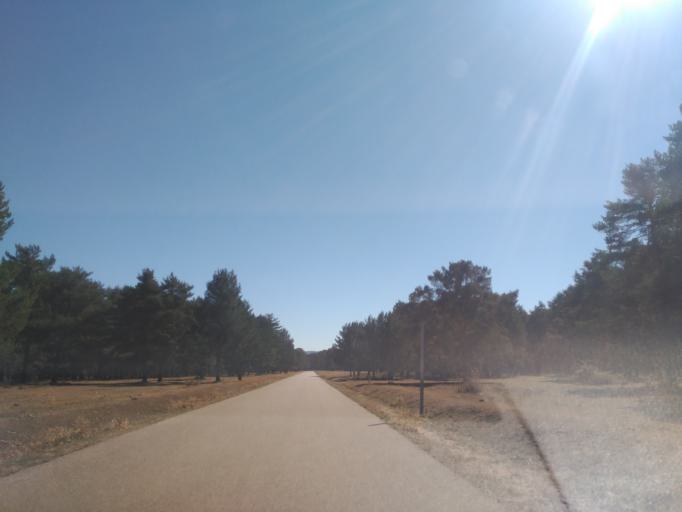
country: ES
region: Castille and Leon
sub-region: Provincia de Soria
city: Vinuesa
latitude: 41.9586
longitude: -2.7844
